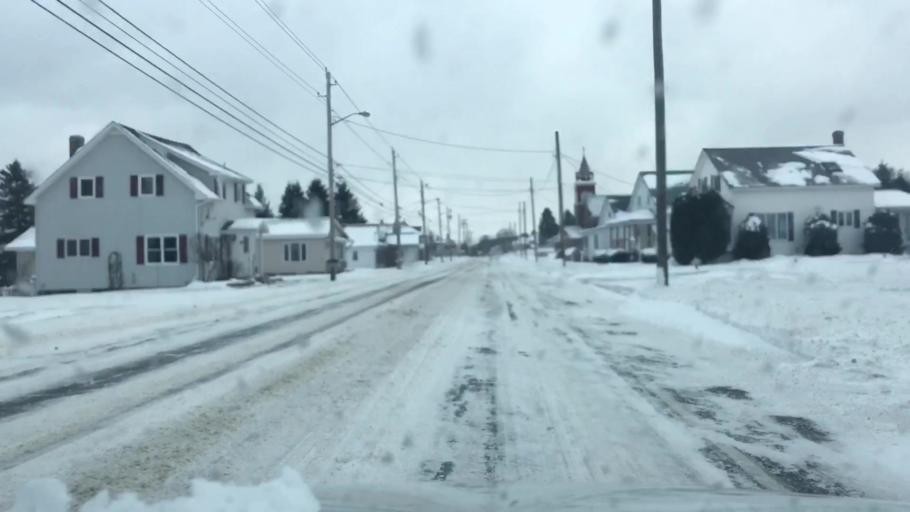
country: US
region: Maine
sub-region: Aroostook County
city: Madawaska
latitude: 47.3098
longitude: -68.1571
